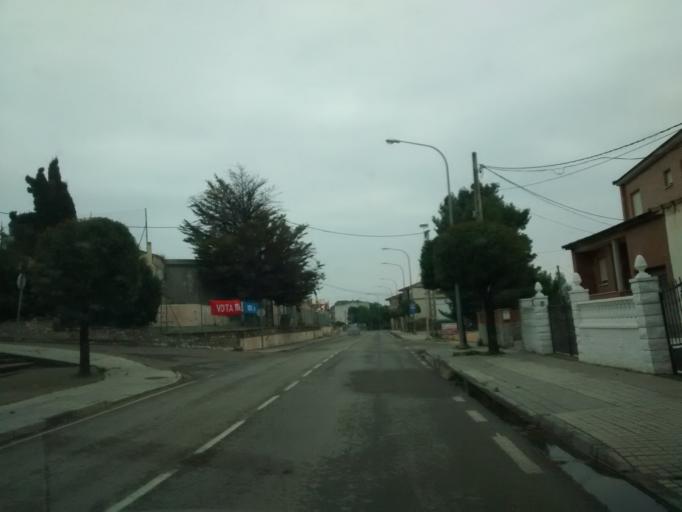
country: ES
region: Aragon
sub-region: Provincia de Zaragoza
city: Caspe
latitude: 41.2305
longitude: -0.0383
